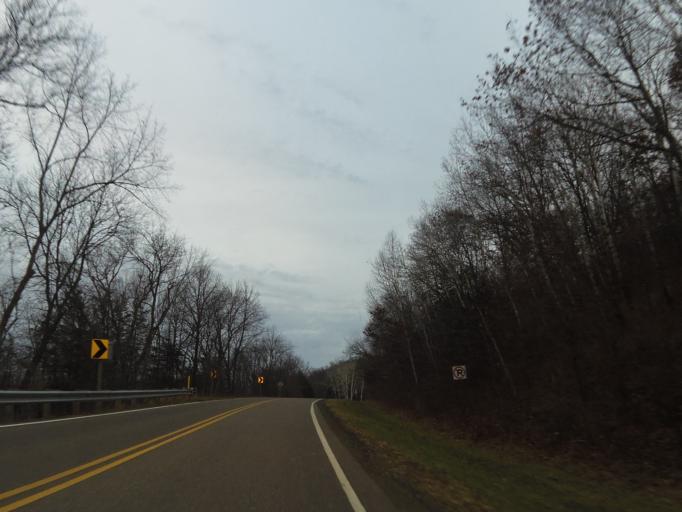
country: US
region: Wisconsin
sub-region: Pierce County
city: River Falls
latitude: 44.8781
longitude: -92.6155
